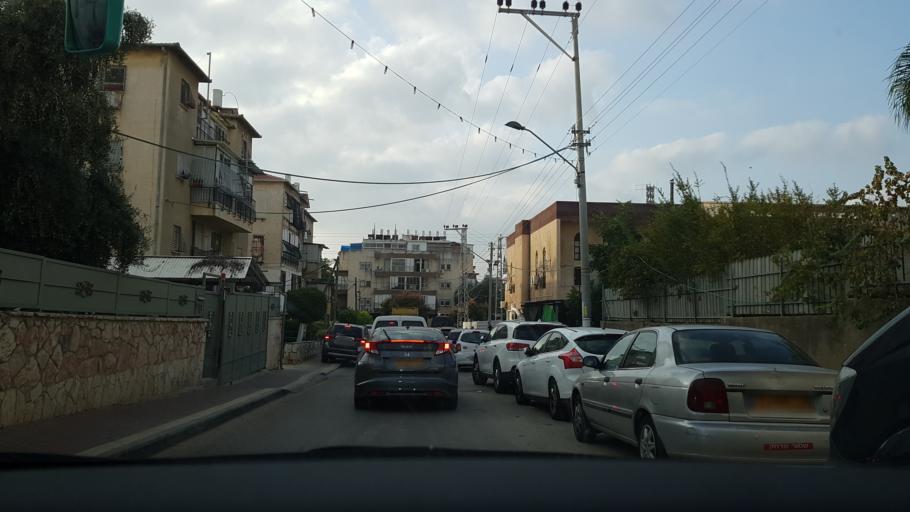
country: IL
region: Central District
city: Ness Ziona
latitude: 31.8945
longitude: 34.8242
